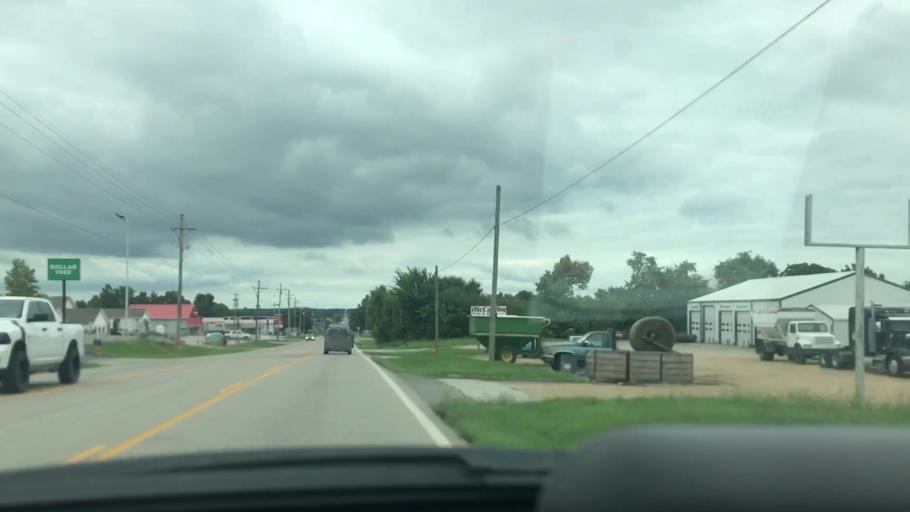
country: US
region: Missouri
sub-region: Dallas County
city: Buffalo
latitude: 37.6422
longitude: -93.1042
